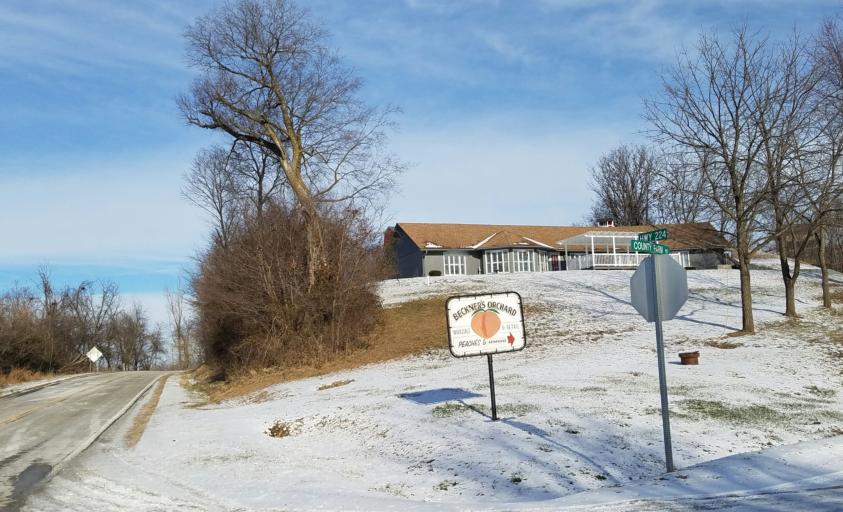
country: US
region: Missouri
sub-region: Lafayette County
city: Lexington
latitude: 39.1447
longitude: -93.9480
